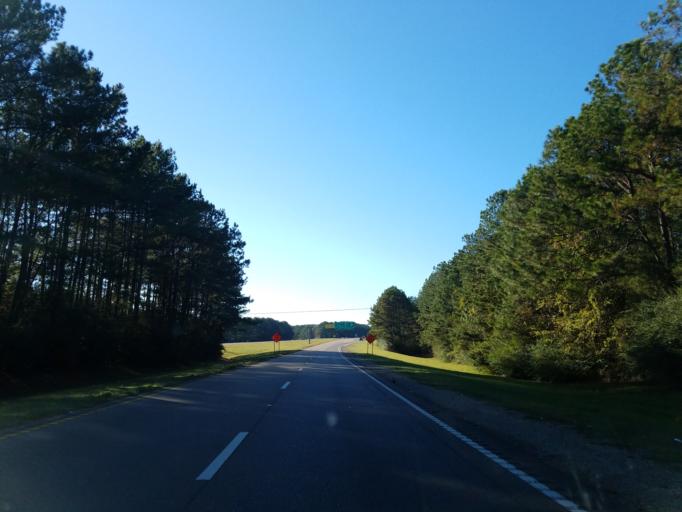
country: US
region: Mississippi
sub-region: Forrest County
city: Hattiesburg
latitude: 31.2383
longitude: -89.3130
